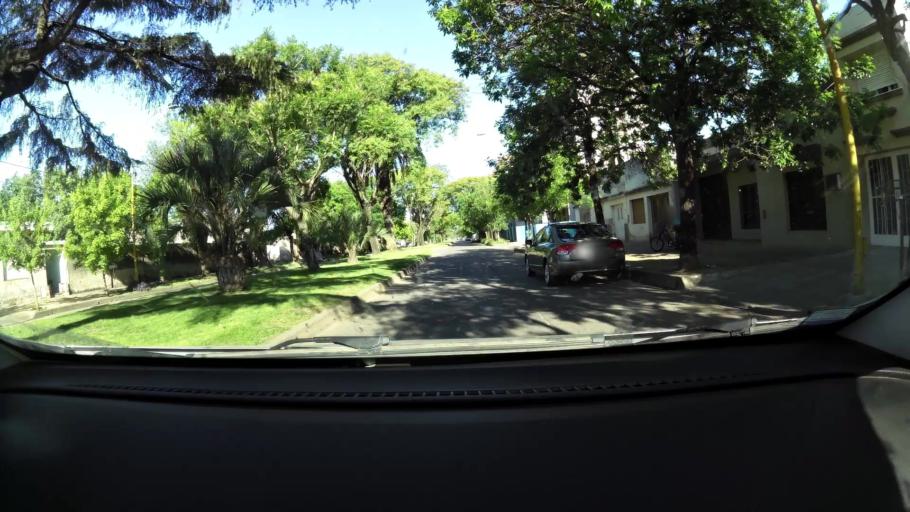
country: AR
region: Cordoba
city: San Francisco
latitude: -31.4321
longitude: -62.0779
